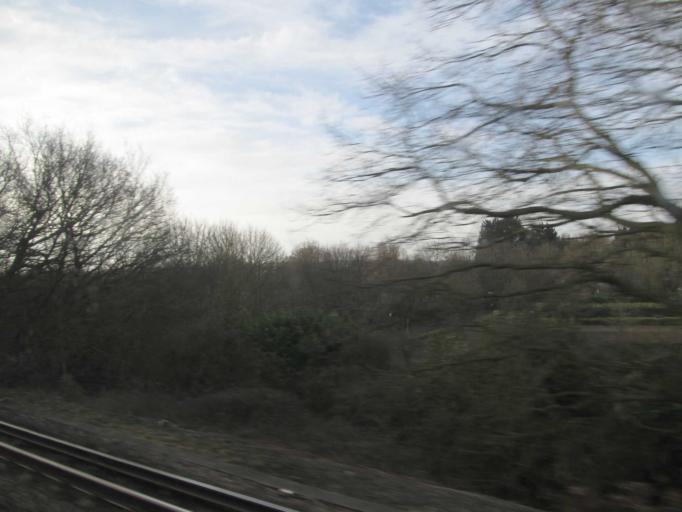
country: GB
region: England
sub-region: Wokingham
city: Woodley
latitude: 51.4379
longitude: -0.8953
